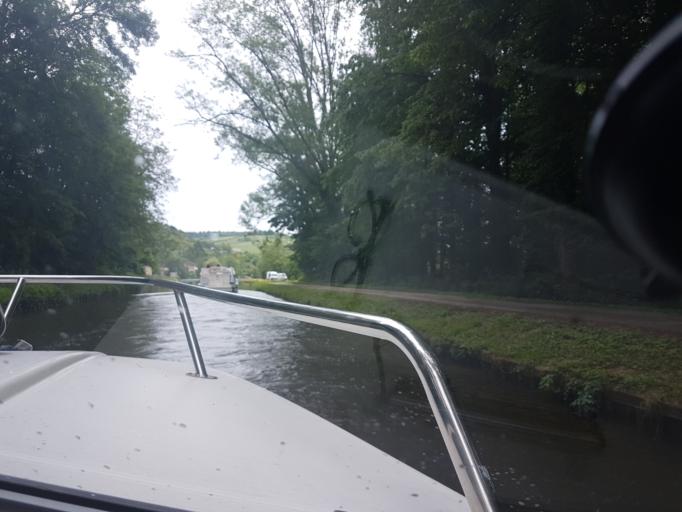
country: FR
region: Bourgogne
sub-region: Departement de l'Yonne
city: Champs-sur-Yonne
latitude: 47.7235
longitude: 3.6203
